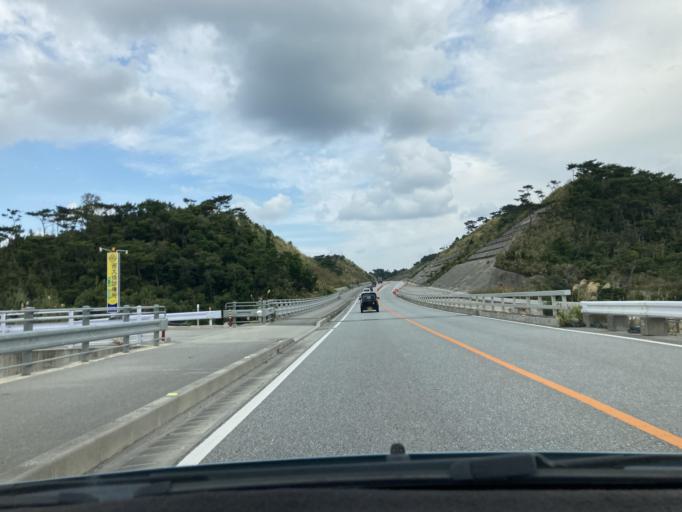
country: JP
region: Okinawa
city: Ishikawa
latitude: 26.4687
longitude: 127.8332
